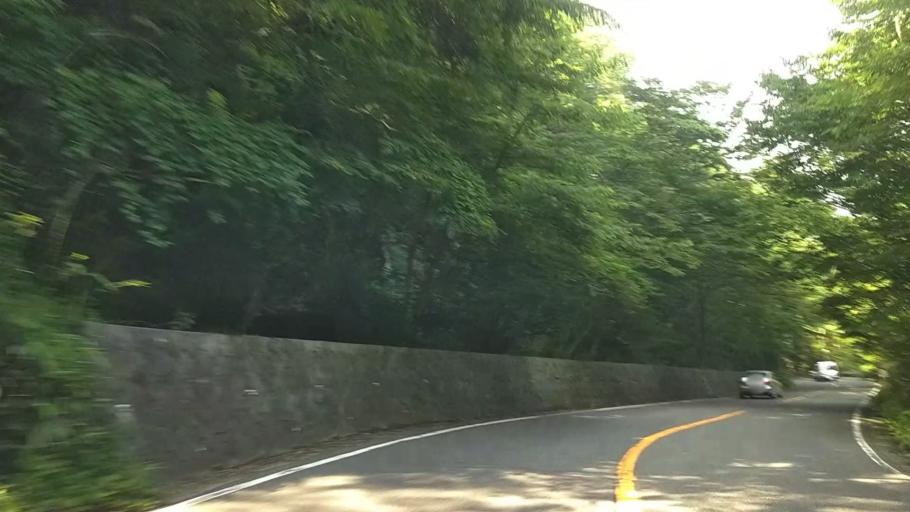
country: JP
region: Kanagawa
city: Hakone
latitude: 35.2242
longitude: 139.0471
